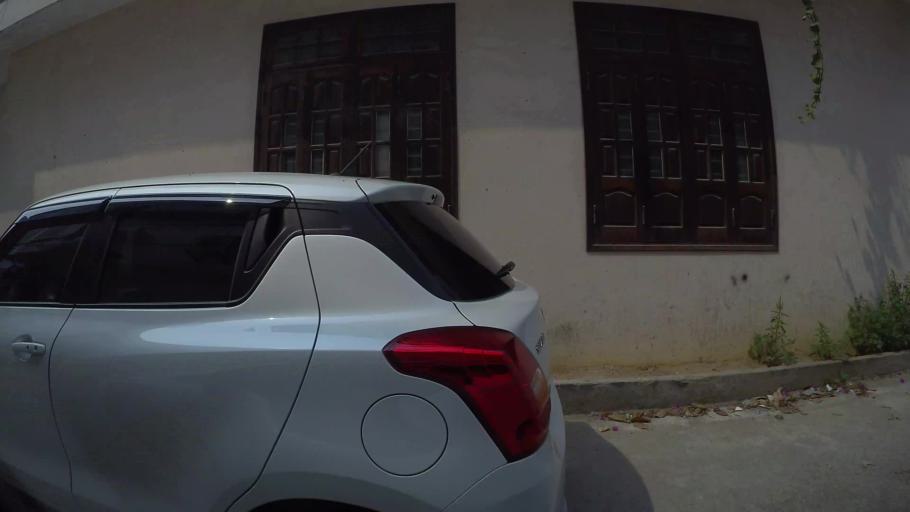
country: VN
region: Da Nang
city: Son Tra
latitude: 16.0417
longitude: 108.2201
